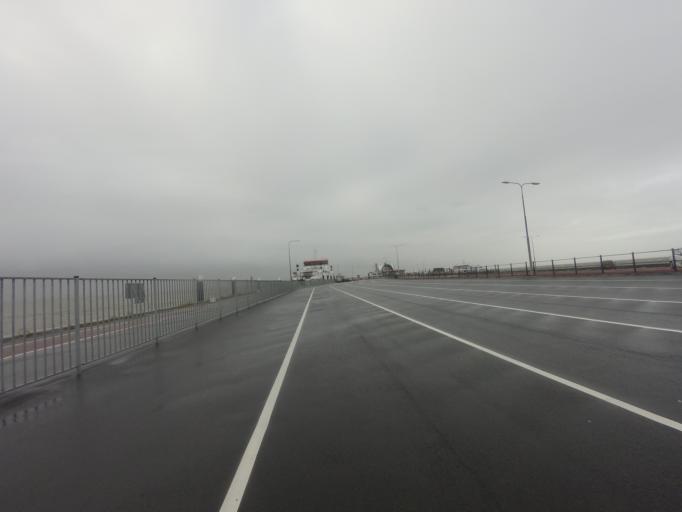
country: NL
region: Friesland
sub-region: Gemeente Ameland
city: Nes
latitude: 53.4356
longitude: 5.7754
